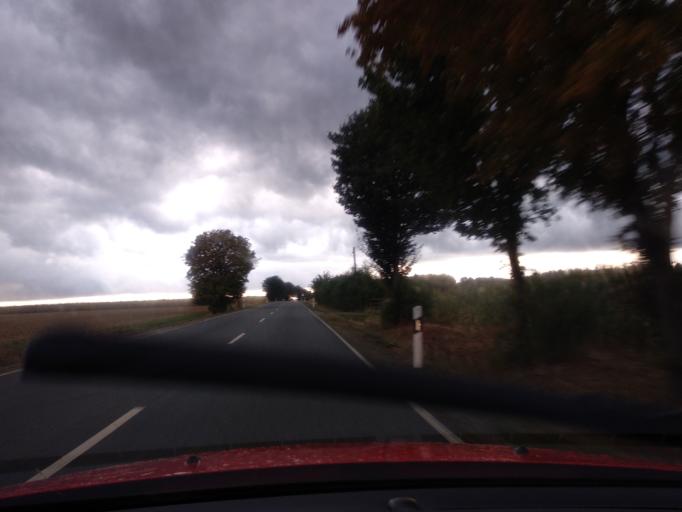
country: DE
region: North Rhine-Westphalia
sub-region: Regierungsbezirk Detmold
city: Willebadessen
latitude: 51.6546
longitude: 9.0940
